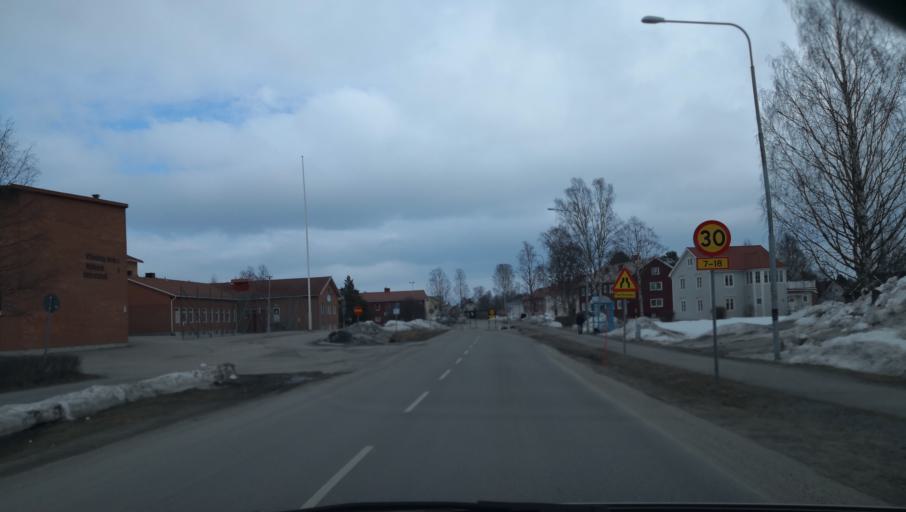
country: SE
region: Vaesterbotten
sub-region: Vannas Kommun
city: Vannasby
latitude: 63.9140
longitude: 19.8127
